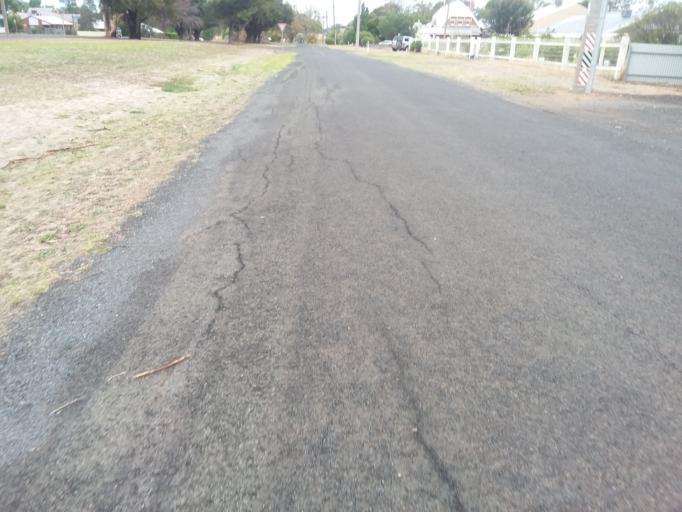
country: AU
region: Victoria
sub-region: Horsham
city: Horsham
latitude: -36.7432
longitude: 141.9377
